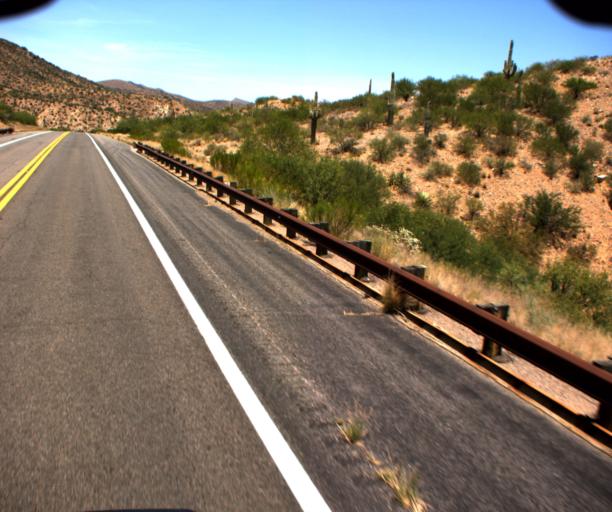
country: US
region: Arizona
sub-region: Gila County
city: Claypool
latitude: 33.4877
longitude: -110.8597
